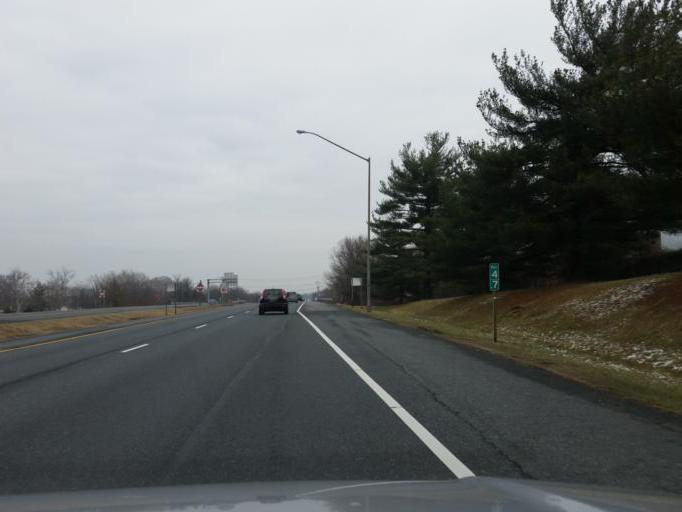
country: US
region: Maryland
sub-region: Baltimore County
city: Baltimore Highlands
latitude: 39.2313
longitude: -76.6458
